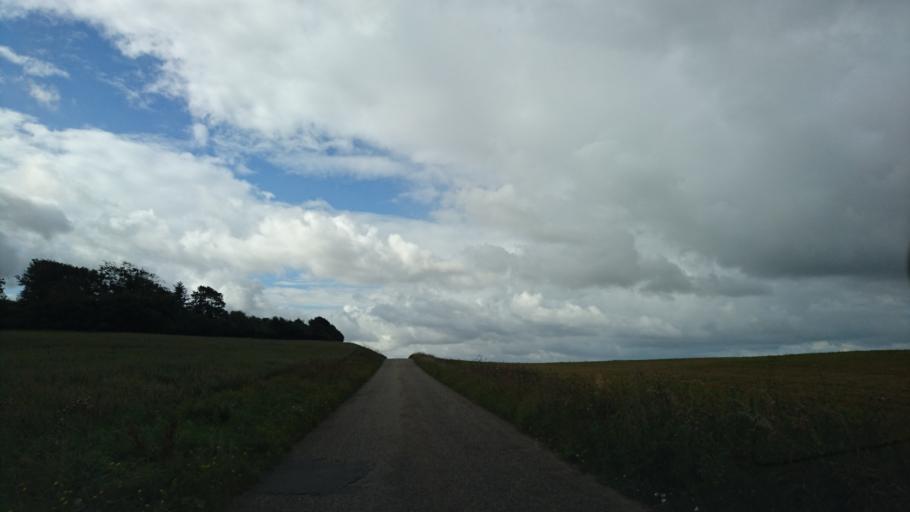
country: DK
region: North Denmark
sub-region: Hjorring Kommune
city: Sindal
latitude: 57.3800
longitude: 10.2439
